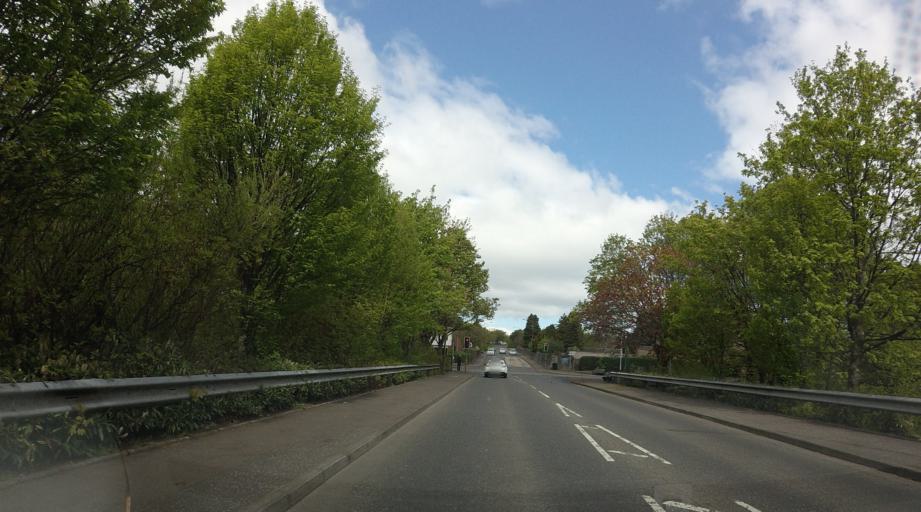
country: GB
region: Scotland
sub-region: West Lothian
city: Broxburn
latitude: 55.9312
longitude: -3.4977
